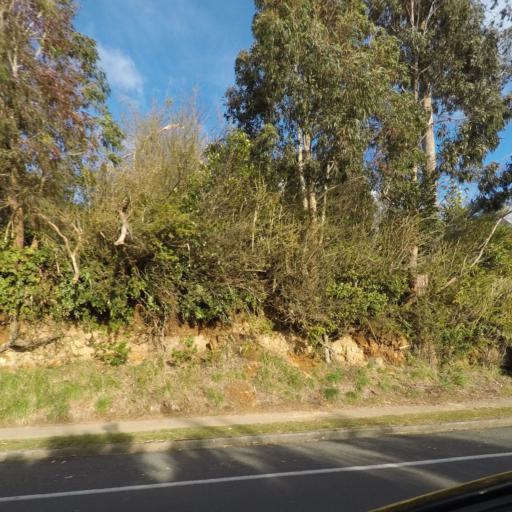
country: NZ
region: Manawatu-Wanganui
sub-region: Ruapehu District
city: Waiouru
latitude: -39.4056
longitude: 175.4100
